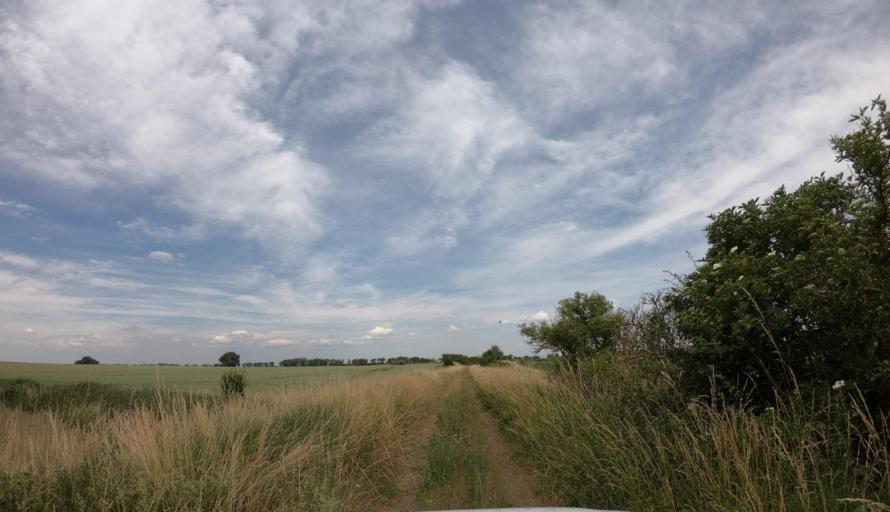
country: PL
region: West Pomeranian Voivodeship
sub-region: Powiat pyrzycki
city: Kozielice
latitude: 53.1306
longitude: 14.8511
